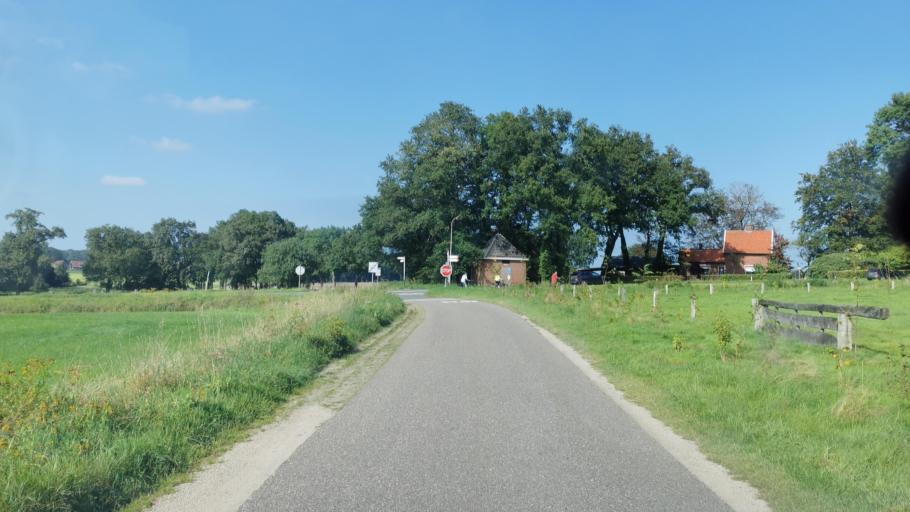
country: DE
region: Lower Saxony
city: Getelo
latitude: 52.4058
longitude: 6.8753
